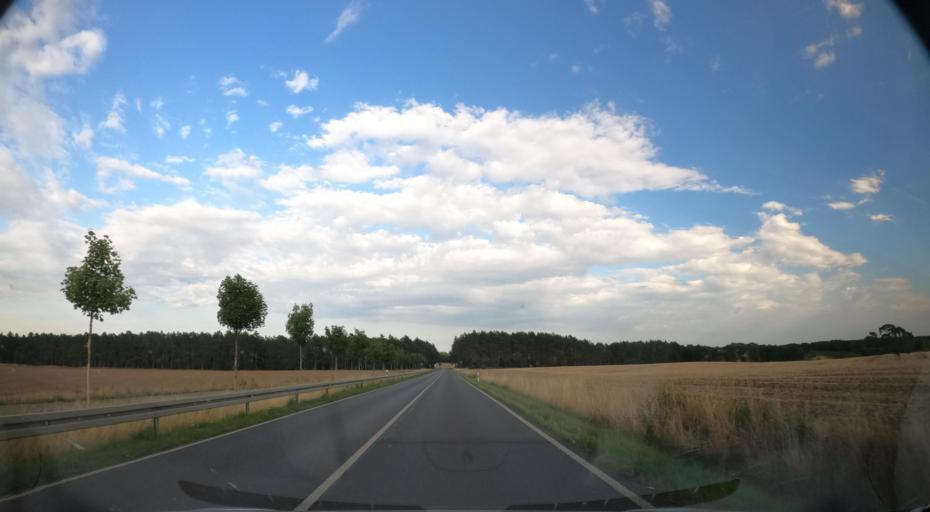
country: PL
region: West Pomeranian Voivodeship
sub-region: Powiat policki
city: Dobra
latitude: 53.4566
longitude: 14.2664
